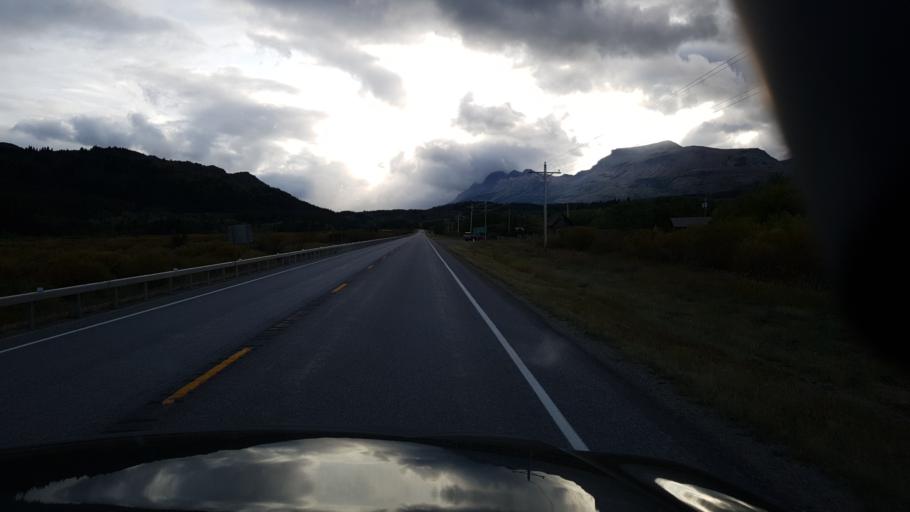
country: US
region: Montana
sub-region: Glacier County
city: South Browning
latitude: 48.4106
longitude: -113.2344
